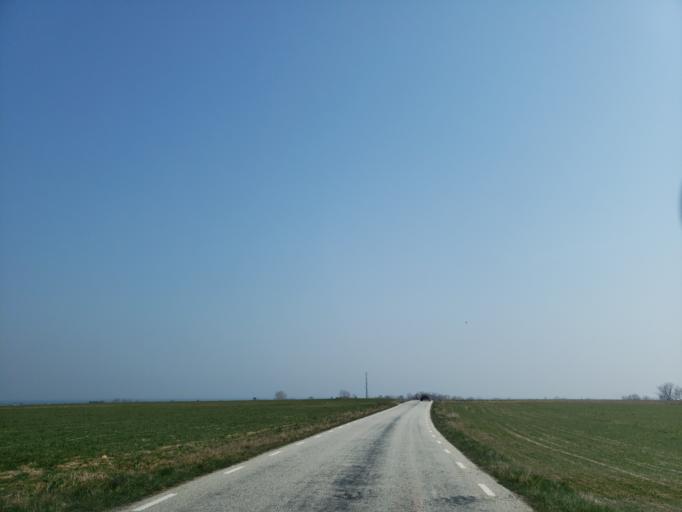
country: SE
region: Skane
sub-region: Simrishamns Kommun
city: Simrishamn
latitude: 55.5112
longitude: 14.3287
